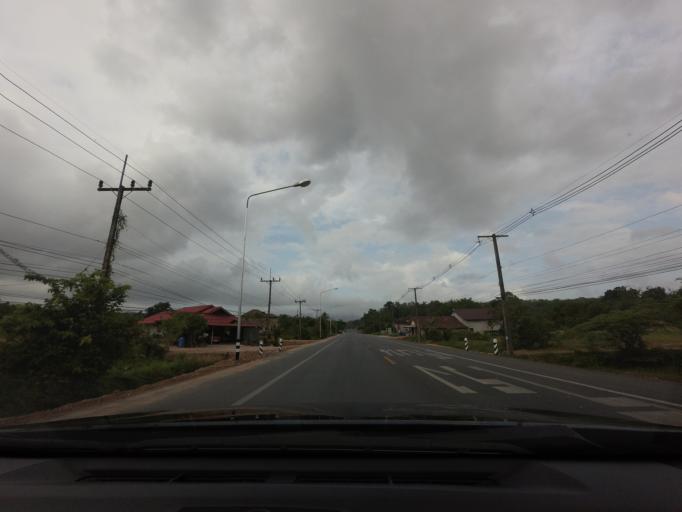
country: TH
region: Yala
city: Raman
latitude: 6.4718
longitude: 101.3971
